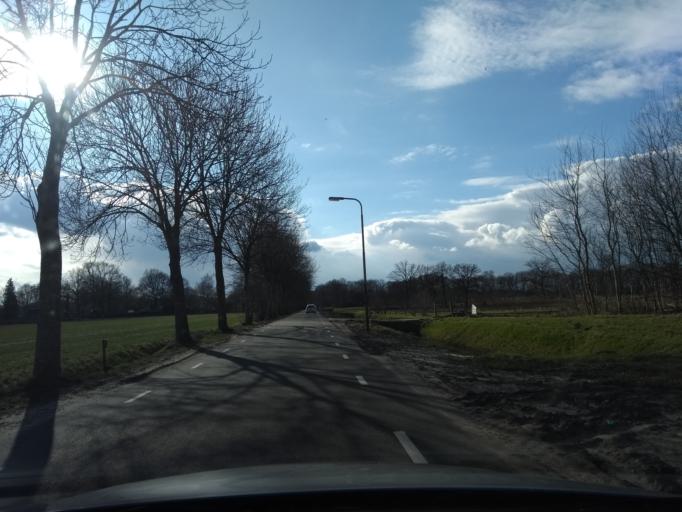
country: NL
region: Drenthe
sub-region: Gemeente De Wolden
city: Ruinen
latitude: 52.7180
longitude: 6.2976
